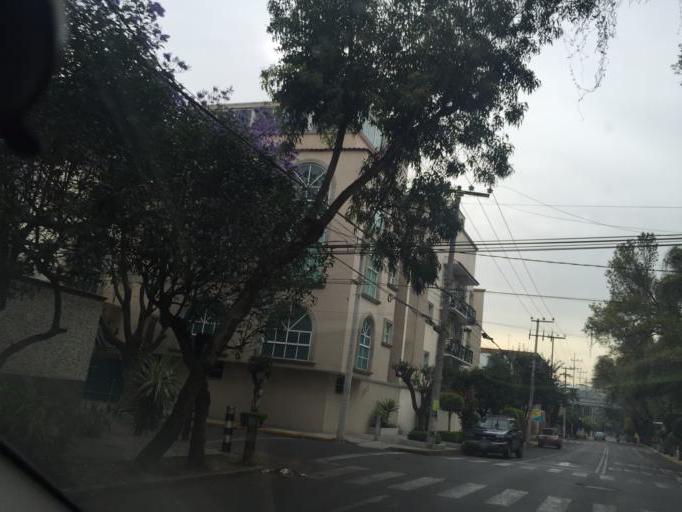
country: MX
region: Mexico
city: Colonia Lindavista
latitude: 19.4920
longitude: -99.1254
